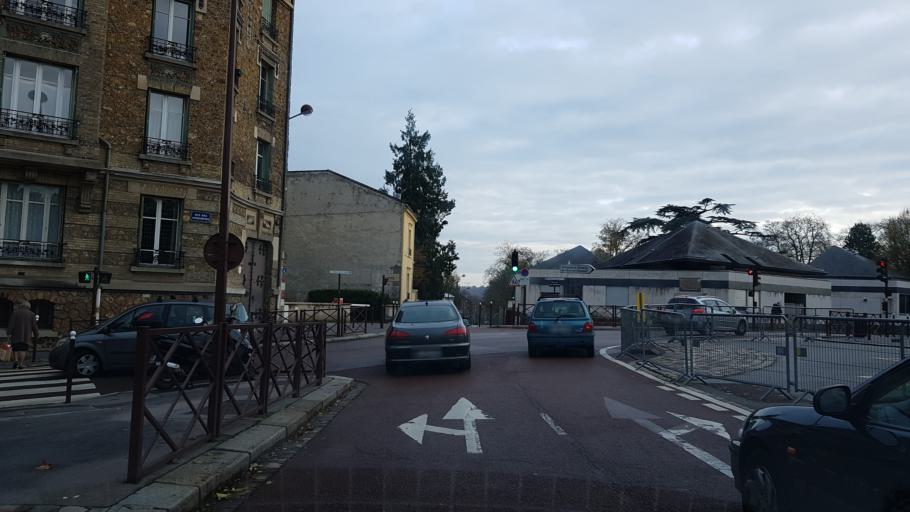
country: FR
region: Ile-de-France
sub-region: Departement des Yvelines
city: Versailles
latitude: 48.8030
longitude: 2.1454
